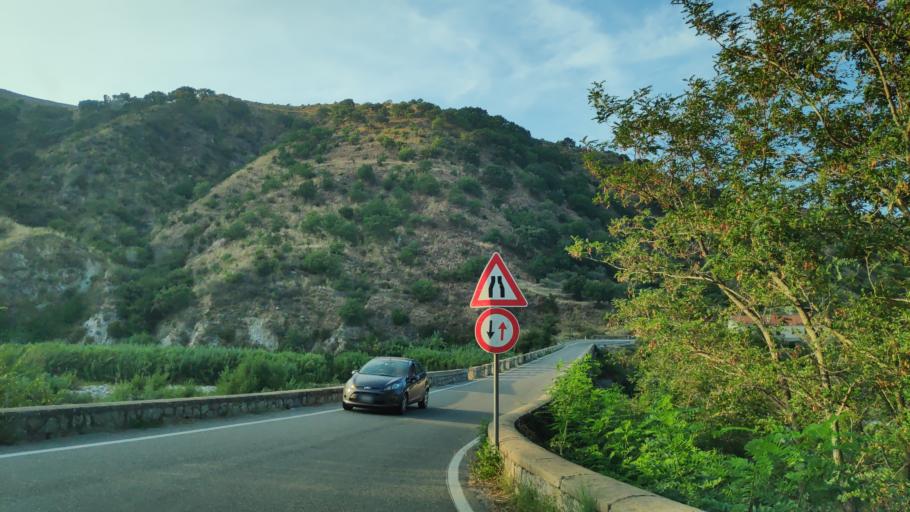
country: IT
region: Calabria
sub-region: Provincia di Catanzaro
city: Satriano
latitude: 38.6726
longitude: 16.4901
